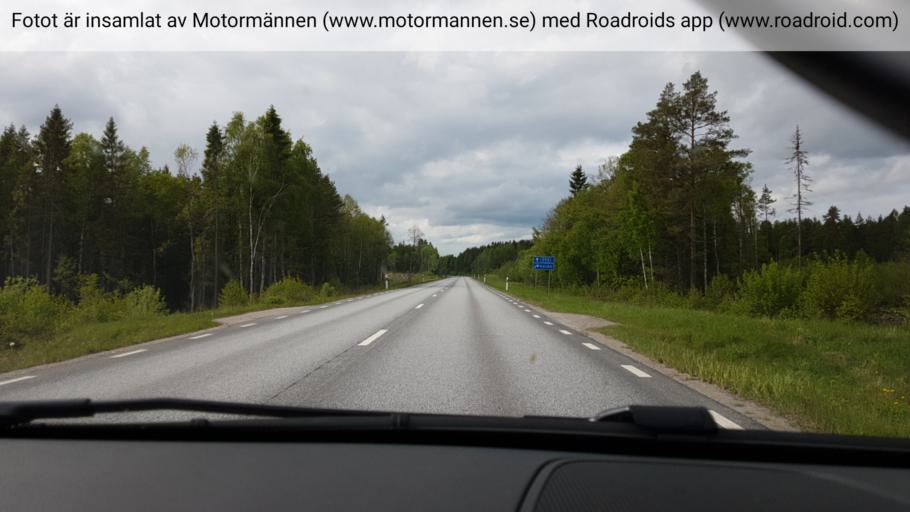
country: SE
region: Uppsala
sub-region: Tierps Kommun
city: Tierp
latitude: 60.3101
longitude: 17.5513
